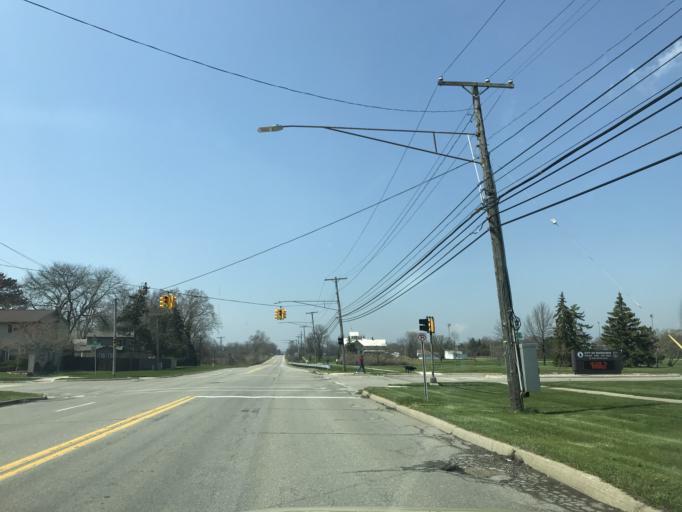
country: US
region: Michigan
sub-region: Wayne County
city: Riverview
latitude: 42.1703
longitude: -83.1937
